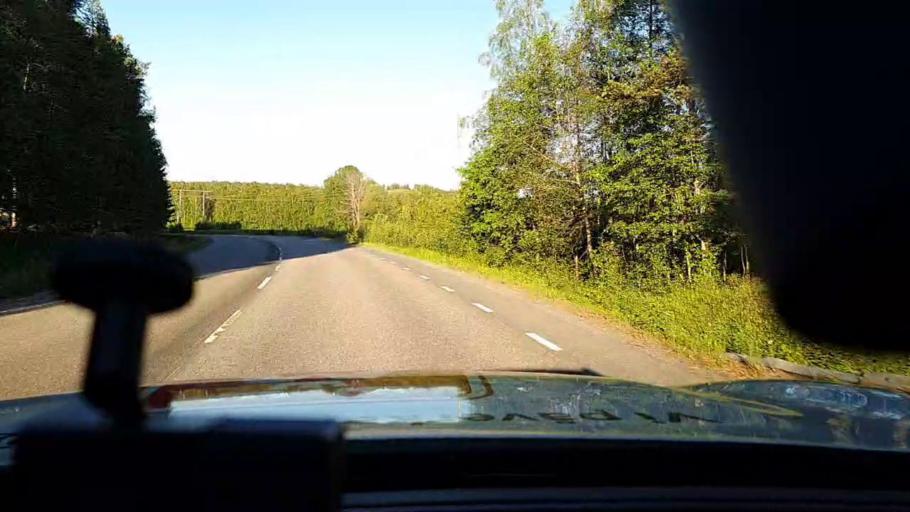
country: SE
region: Norrbotten
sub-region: Lulea Kommun
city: Lulea
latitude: 65.6073
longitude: 22.1720
